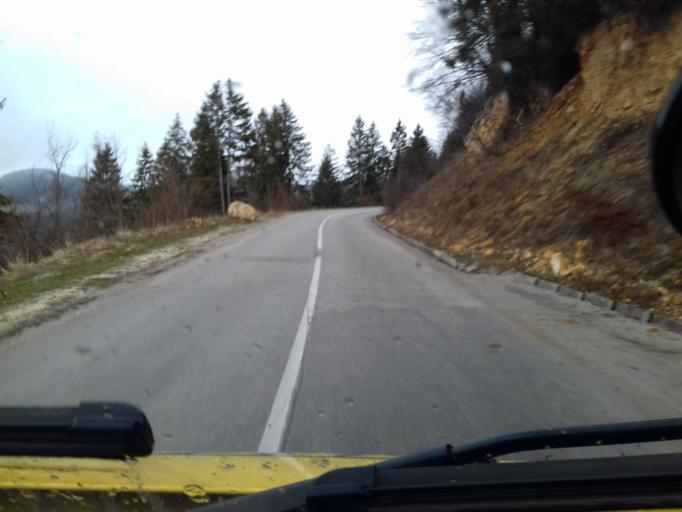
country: BA
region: Federation of Bosnia and Herzegovina
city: Turbe
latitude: 44.2735
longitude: 17.5134
